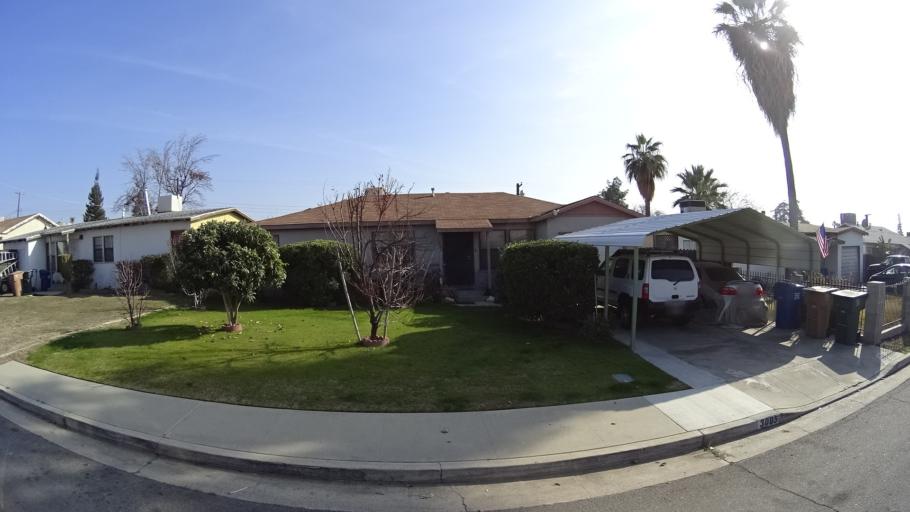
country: US
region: California
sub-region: Kern County
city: Bakersfield
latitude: 35.3892
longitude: -118.9561
